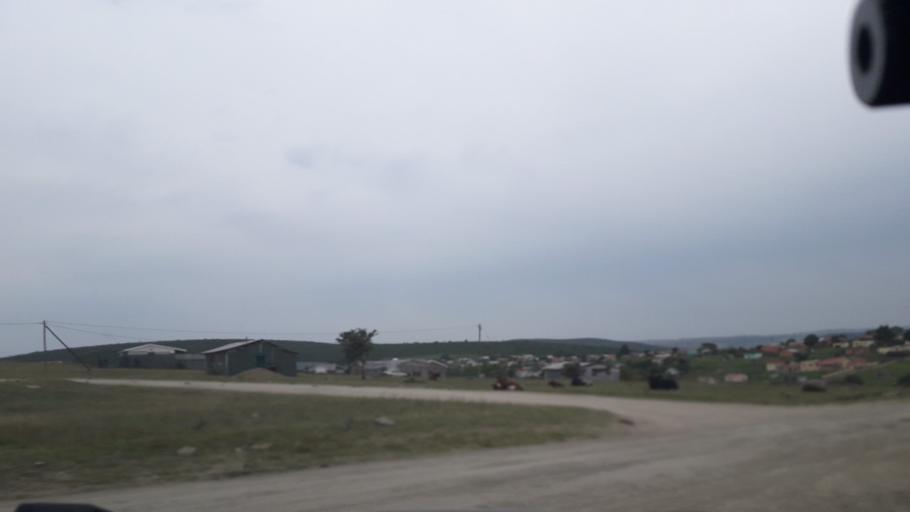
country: ZA
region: Eastern Cape
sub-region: Buffalo City Metropolitan Municipality
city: Bhisho
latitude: -32.7958
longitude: 27.3451
